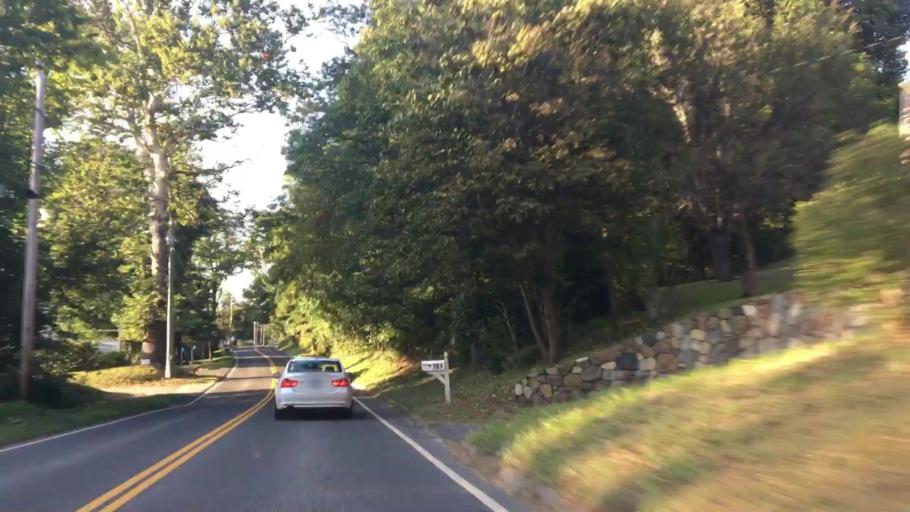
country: US
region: Connecticut
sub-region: Litchfield County
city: New Milford
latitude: 41.5645
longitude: -73.4048
